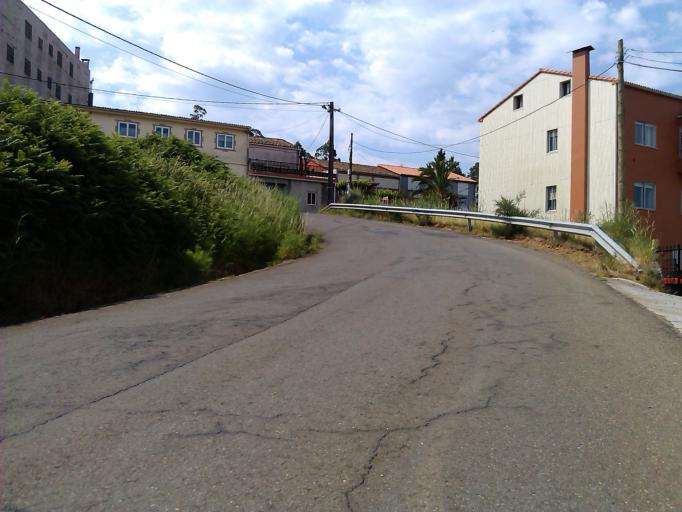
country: ES
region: Galicia
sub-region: Provincia da Coruna
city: Santiago de Compostela
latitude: 42.8878
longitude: -8.5039
